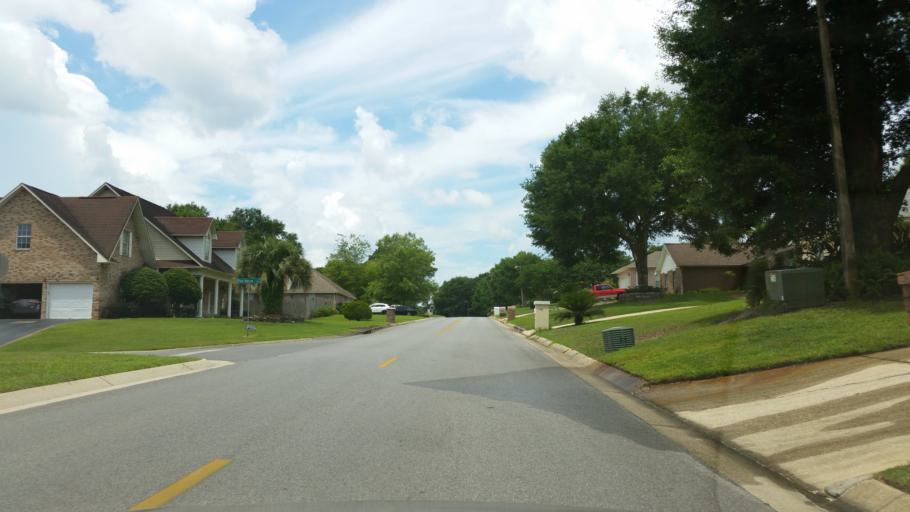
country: US
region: Florida
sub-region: Escambia County
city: Brent
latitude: 30.4785
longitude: -87.2702
